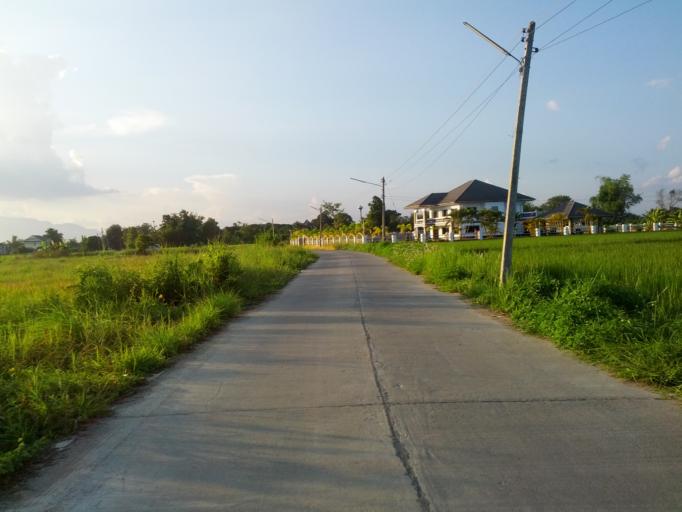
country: TH
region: Chiang Mai
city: San Kamphaeng
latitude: 18.7669
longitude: 99.0990
